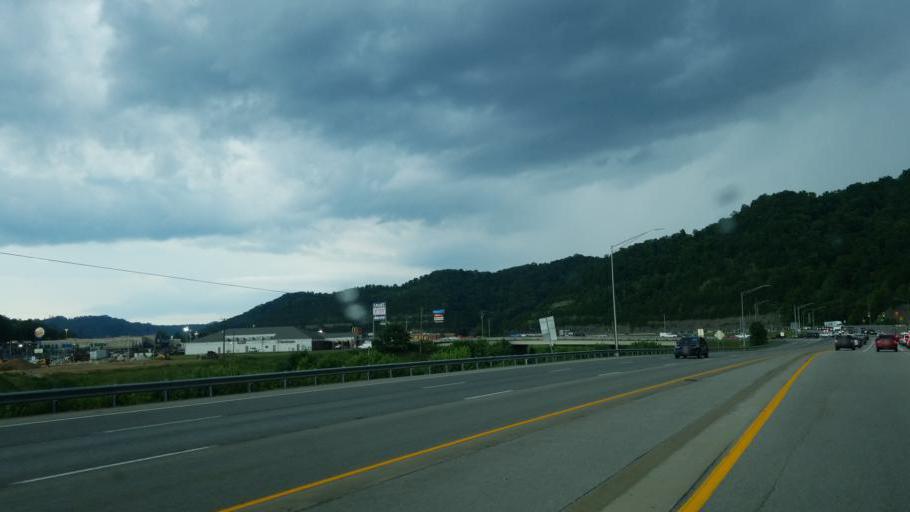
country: US
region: Kentucky
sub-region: Pike County
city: Pikeville
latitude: 37.5015
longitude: -82.5319
